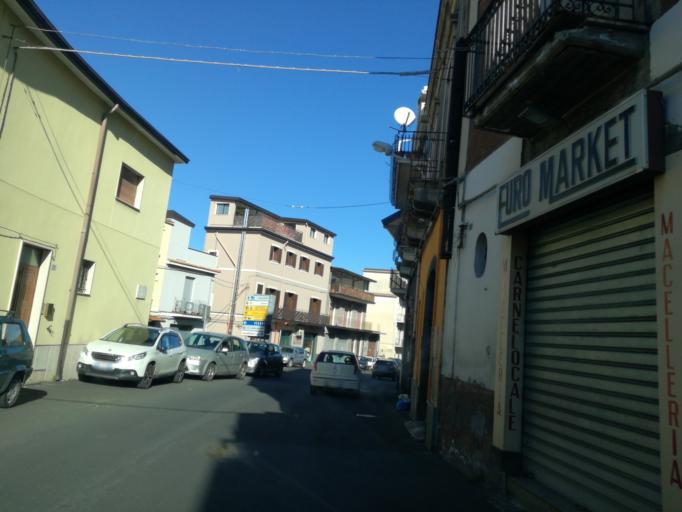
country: IT
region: Sicily
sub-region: Catania
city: Bronte
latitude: 37.7888
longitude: 14.8381
